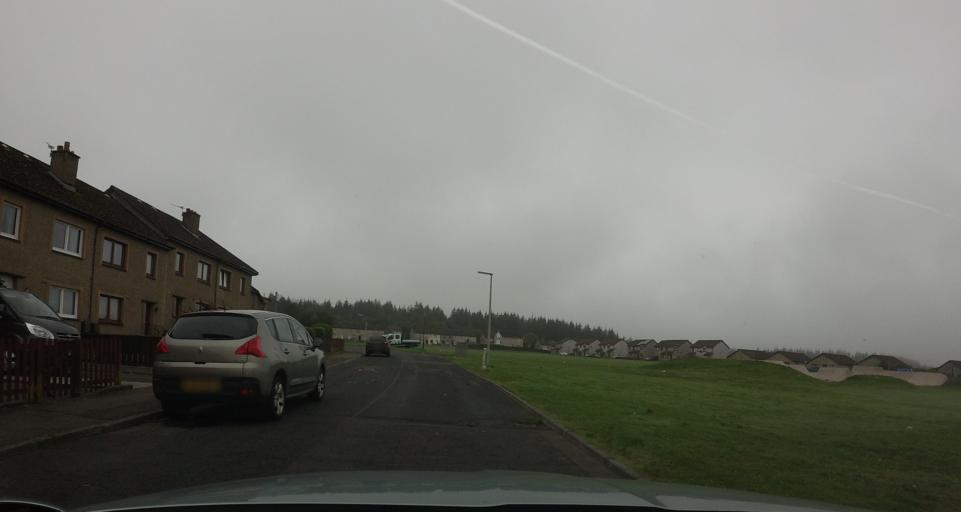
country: GB
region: Scotland
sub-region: Fife
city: Kelty
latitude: 56.1350
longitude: -3.3922
